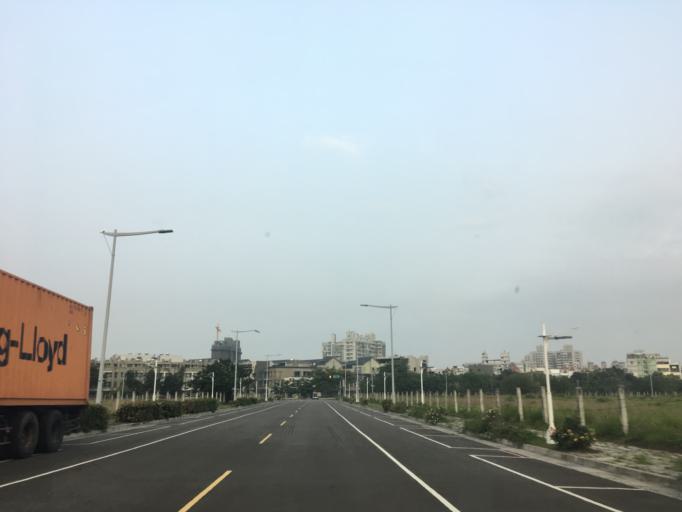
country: TW
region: Taiwan
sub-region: Taichung City
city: Taichung
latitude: 24.1954
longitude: 120.6671
